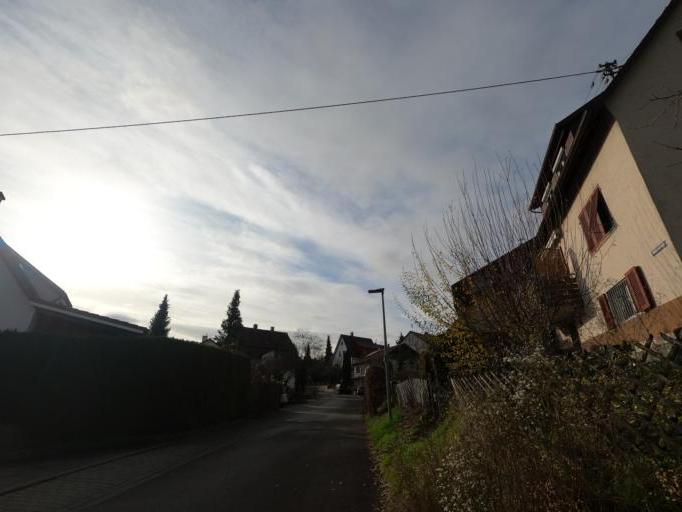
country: DE
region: Baden-Wuerttemberg
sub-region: Regierungsbezirk Stuttgart
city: Albershausen
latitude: 48.6991
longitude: 9.5693
